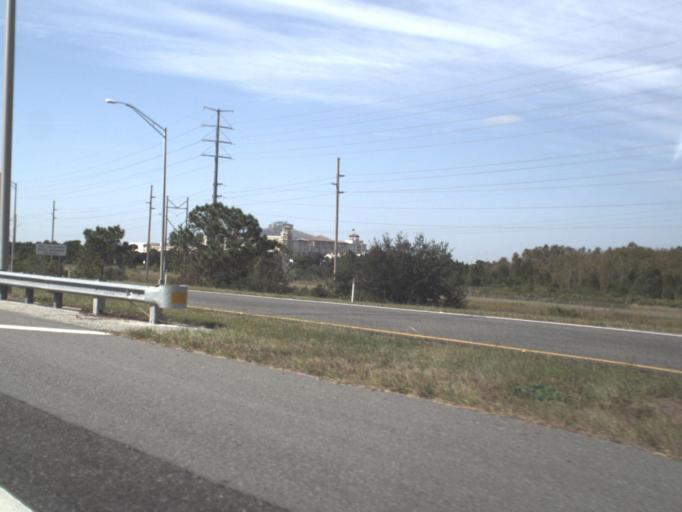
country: US
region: Florida
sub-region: Osceola County
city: Celebration
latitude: 28.3448
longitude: -81.5146
